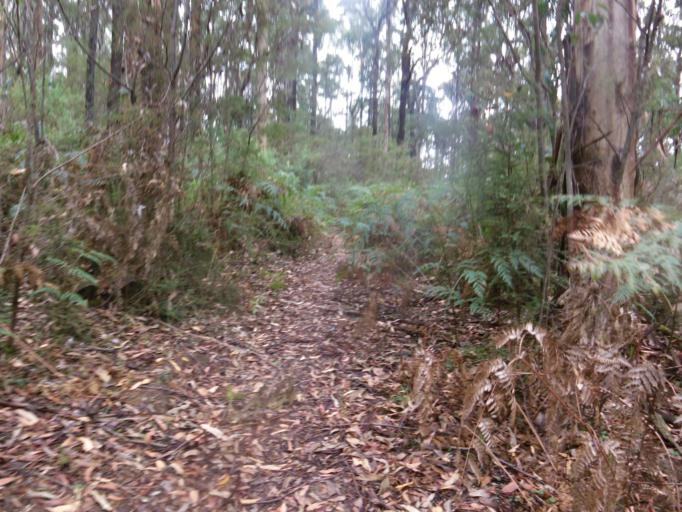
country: AU
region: Victoria
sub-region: Nillumbik
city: Saint Andrews
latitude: -37.5377
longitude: 145.3491
